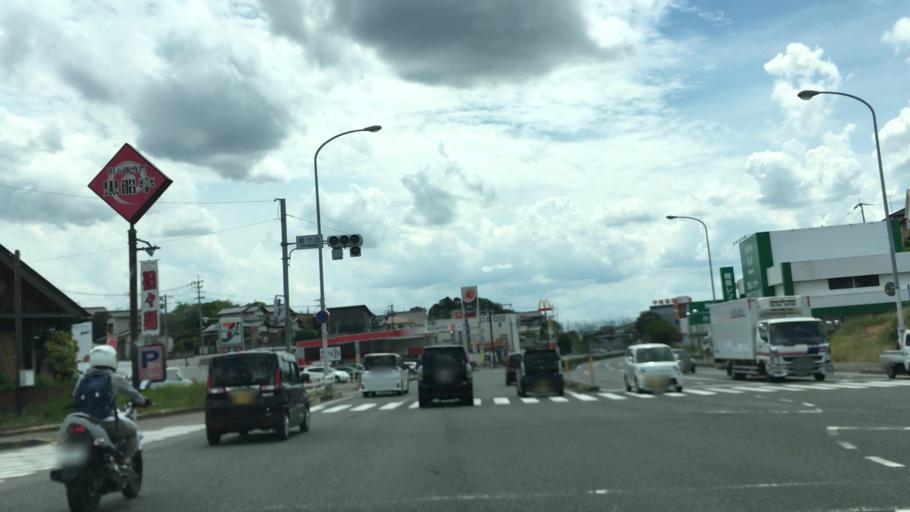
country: JP
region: Fukuoka
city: Dazaifu
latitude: 33.5034
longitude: 130.5311
